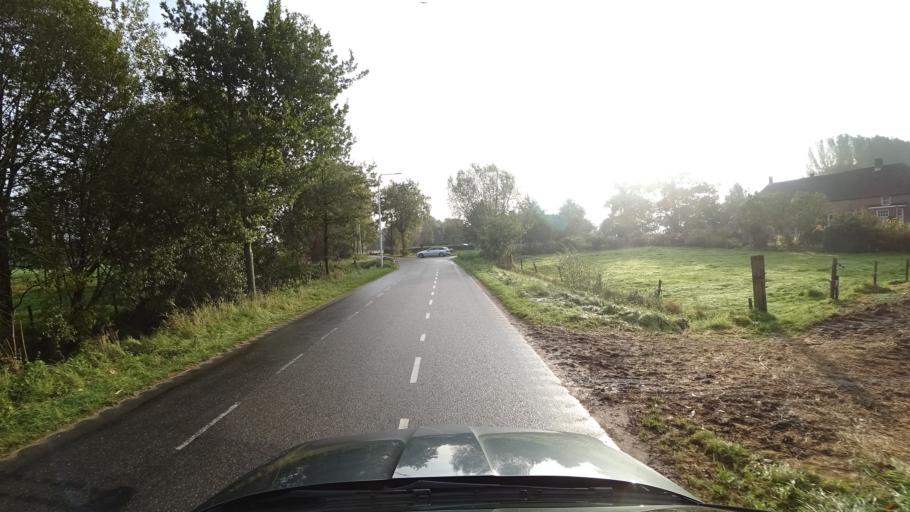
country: NL
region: Gelderland
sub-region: Gemeente Ede
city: Bennekom
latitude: 51.9969
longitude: 5.6396
